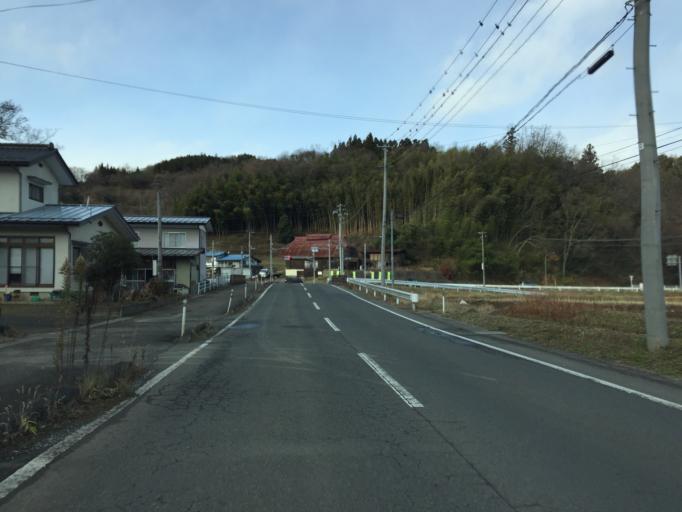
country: JP
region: Fukushima
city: Hobaramachi
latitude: 37.7563
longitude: 140.5594
